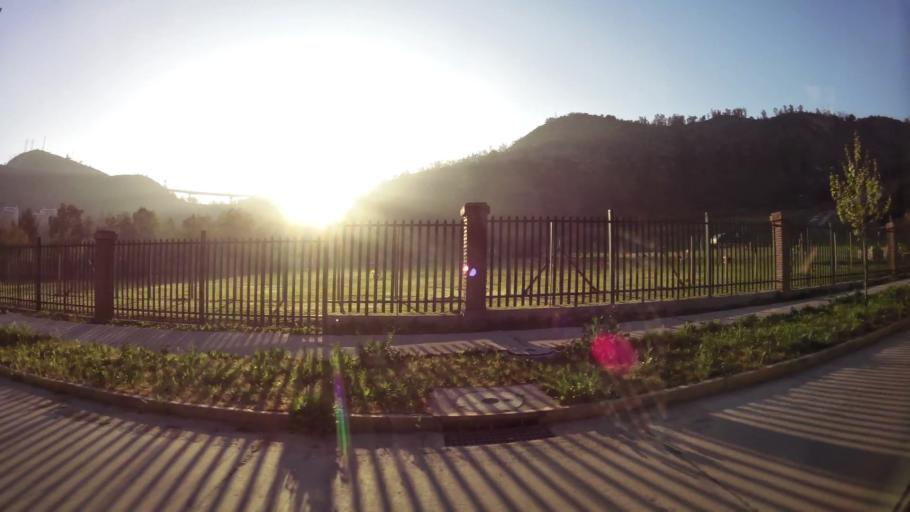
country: CL
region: Santiago Metropolitan
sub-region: Provincia de Santiago
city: Santiago
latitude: -33.3901
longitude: -70.6115
